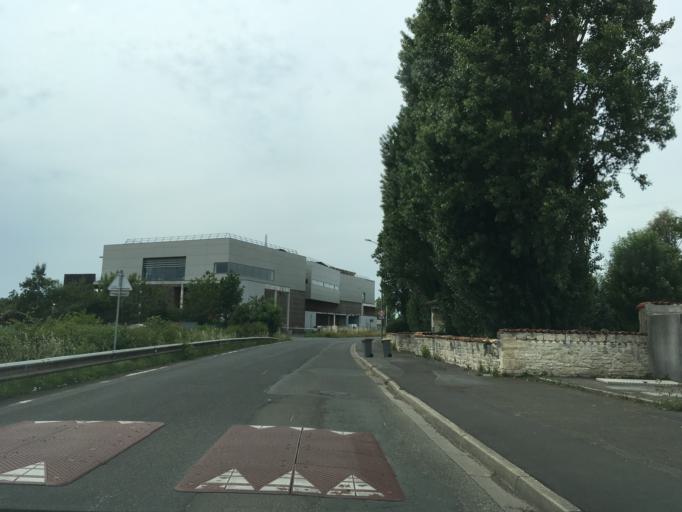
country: FR
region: Poitou-Charentes
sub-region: Departement des Deux-Sevres
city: Niort
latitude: 46.3084
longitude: -0.4780
